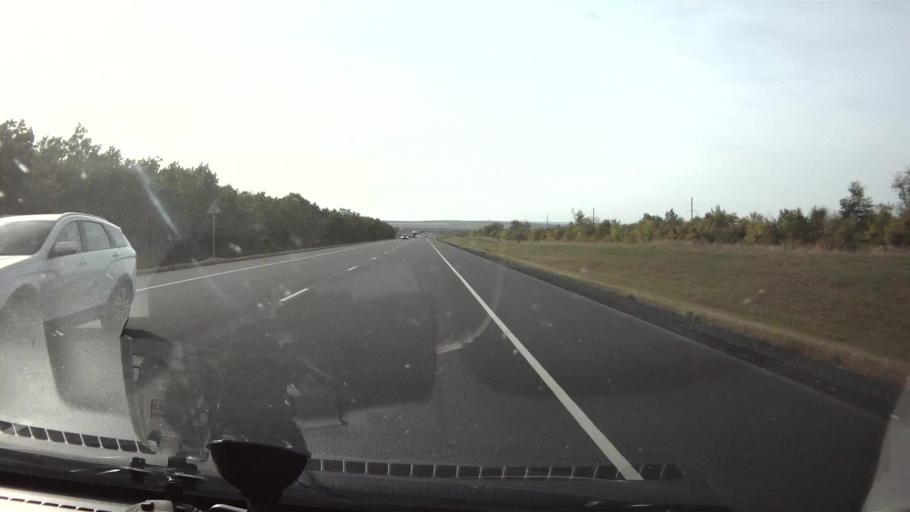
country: RU
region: Saratov
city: Yelshanka
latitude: 51.8265
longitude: 46.2802
